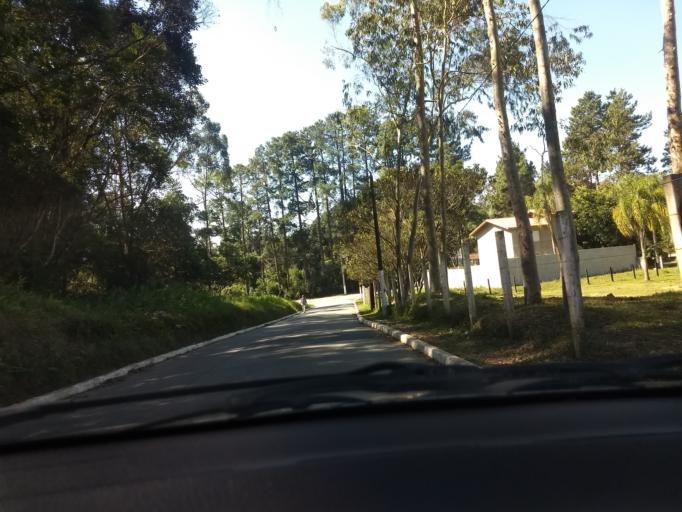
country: BR
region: Sao Paulo
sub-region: Embu-Guacu
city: Embu Guacu
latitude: -23.8404
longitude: -46.7332
